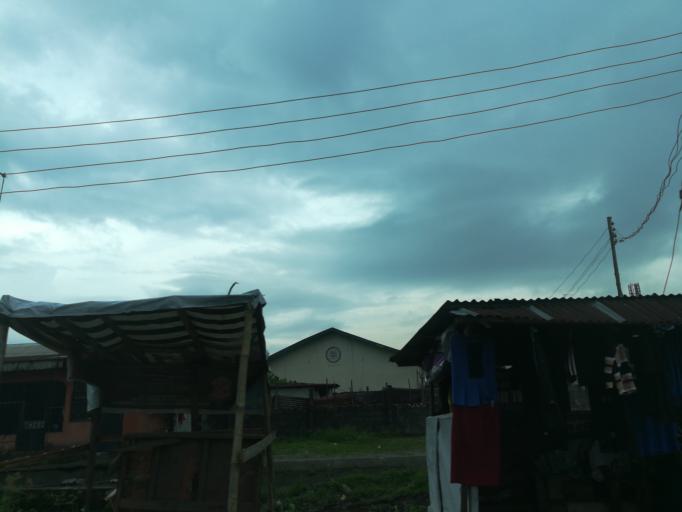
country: NG
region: Rivers
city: Port Harcourt
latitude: 4.8171
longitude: 7.0159
